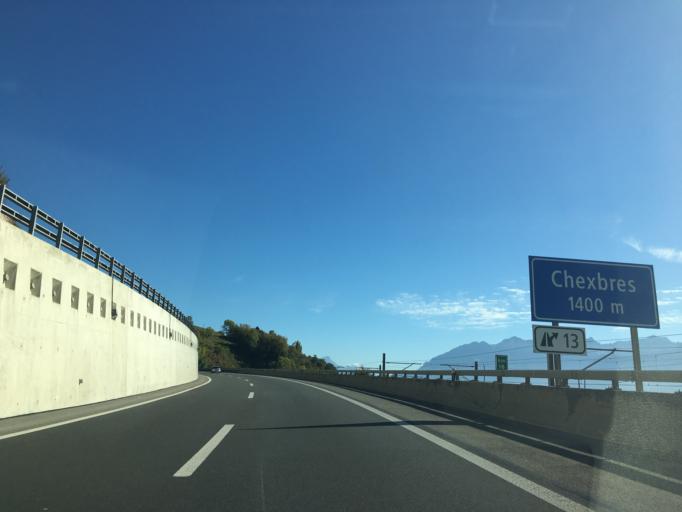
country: CH
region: Vaud
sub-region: Lavaux-Oron District
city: Cully
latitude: 46.4945
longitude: 6.7503
